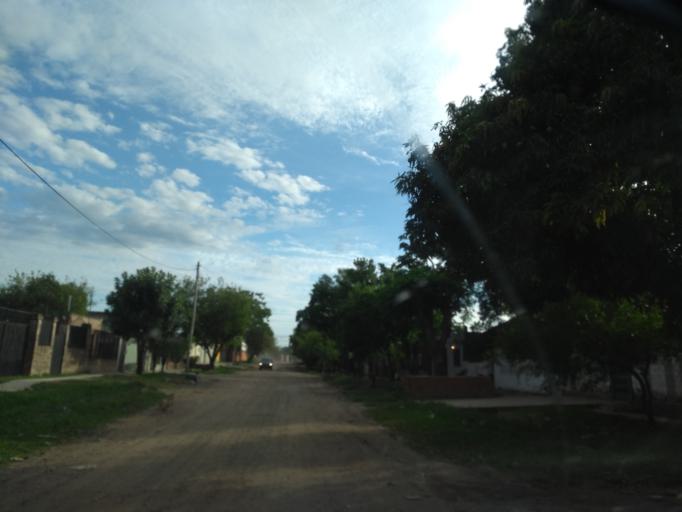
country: AR
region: Chaco
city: Resistencia
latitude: -27.4541
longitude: -58.9669
